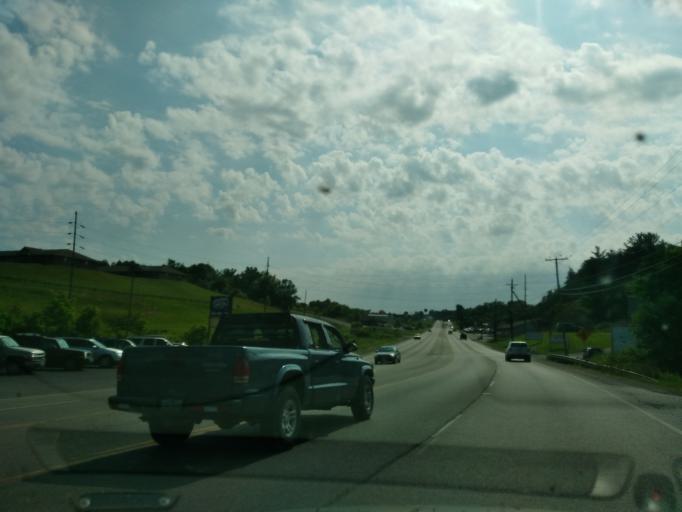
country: US
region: Ohio
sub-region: Muskingum County
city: South Zanesville
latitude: 39.9000
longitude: -82.0274
